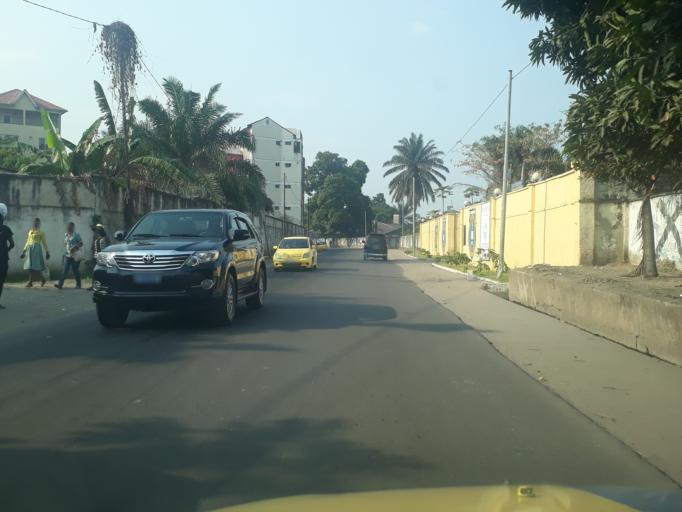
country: CD
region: Kinshasa
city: Kinshasa
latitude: -4.3161
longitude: 15.3308
